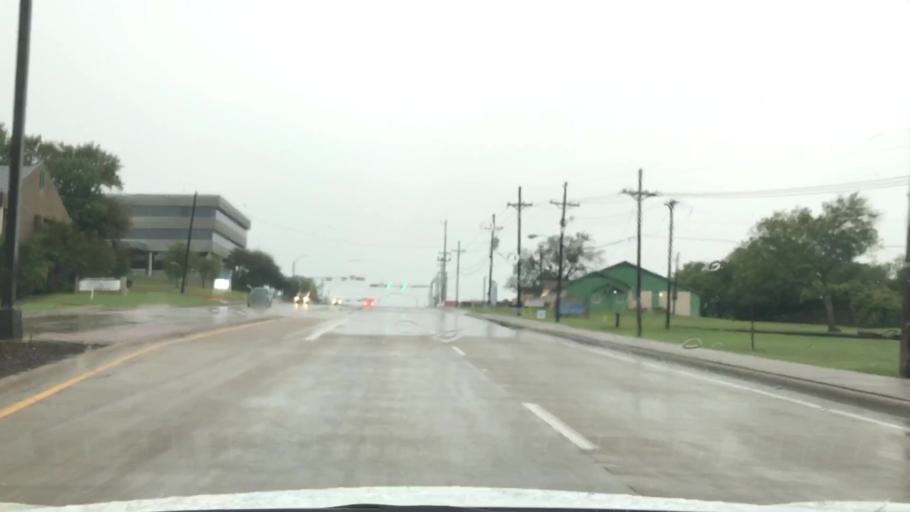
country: US
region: Texas
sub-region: Rockwall County
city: Rockwall
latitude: 32.9035
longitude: -96.4643
